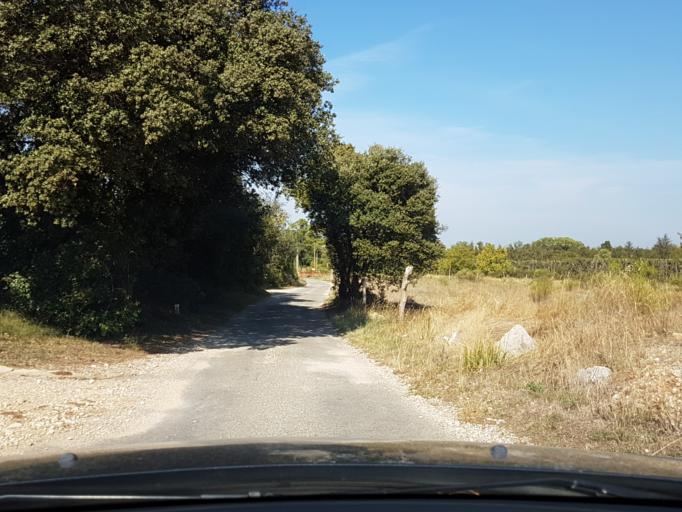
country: FR
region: Provence-Alpes-Cote d'Azur
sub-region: Departement des Bouches-du-Rhone
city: Eygalieres
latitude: 43.7708
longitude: 4.9544
